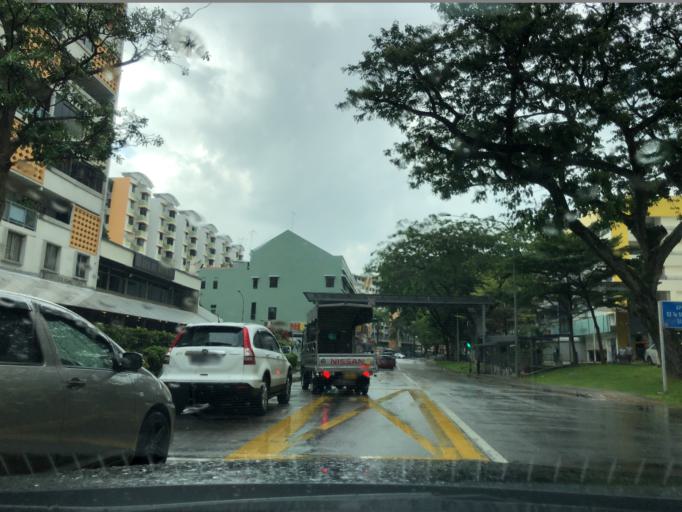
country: SG
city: Singapore
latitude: 1.2890
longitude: 103.8288
